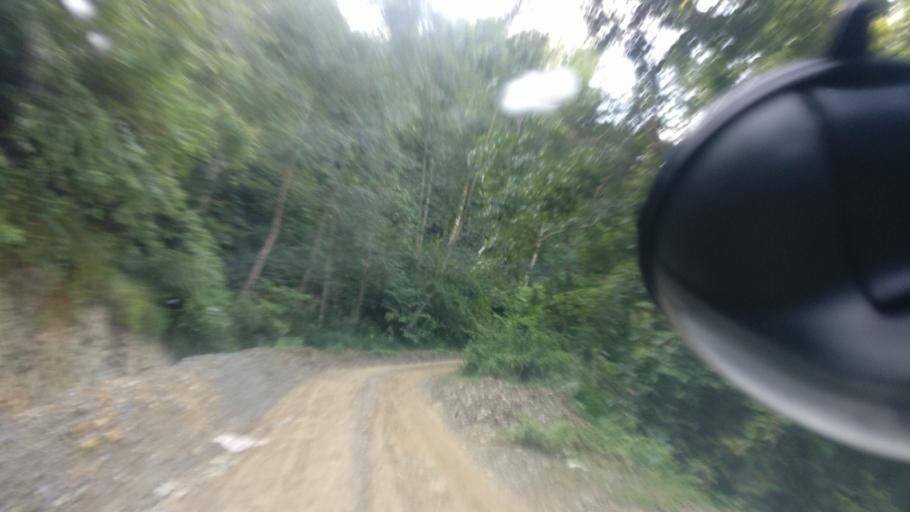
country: NP
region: Western Region
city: Baglung
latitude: 28.1541
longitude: 83.6539
